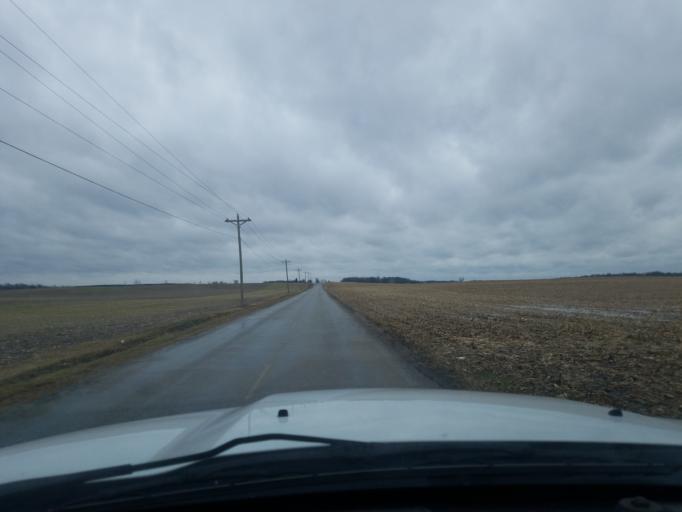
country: US
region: Indiana
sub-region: Noble County
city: Albion
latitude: 41.4372
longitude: -85.3947
